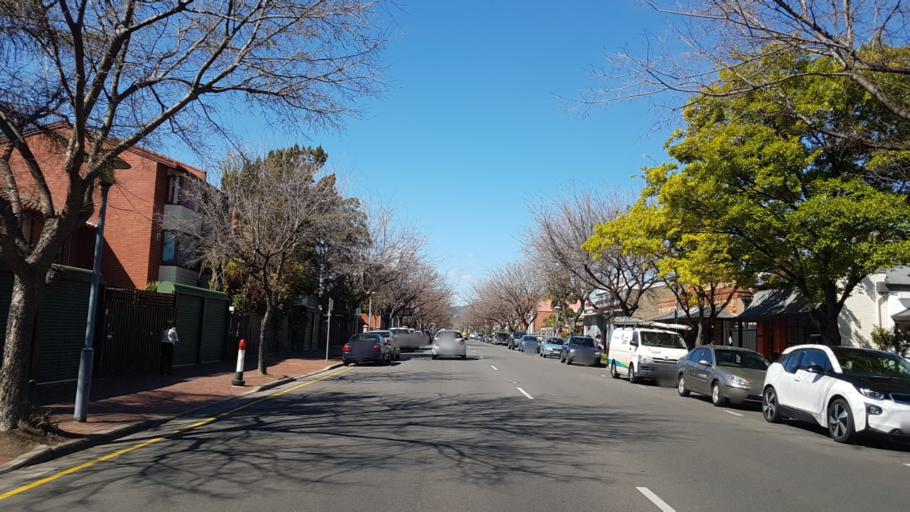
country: AU
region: South Australia
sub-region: Adelaide
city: Adelaide
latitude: -34.9310
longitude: 138.6091
